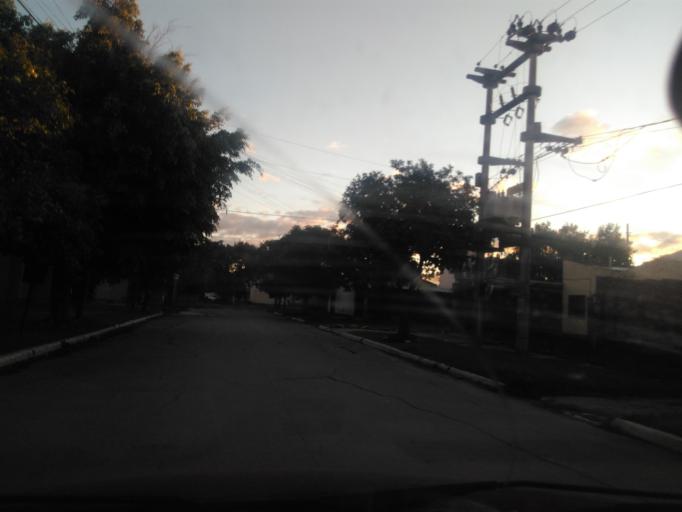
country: AR
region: Chaco
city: Resistencia
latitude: -27.4561
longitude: -59.0134
